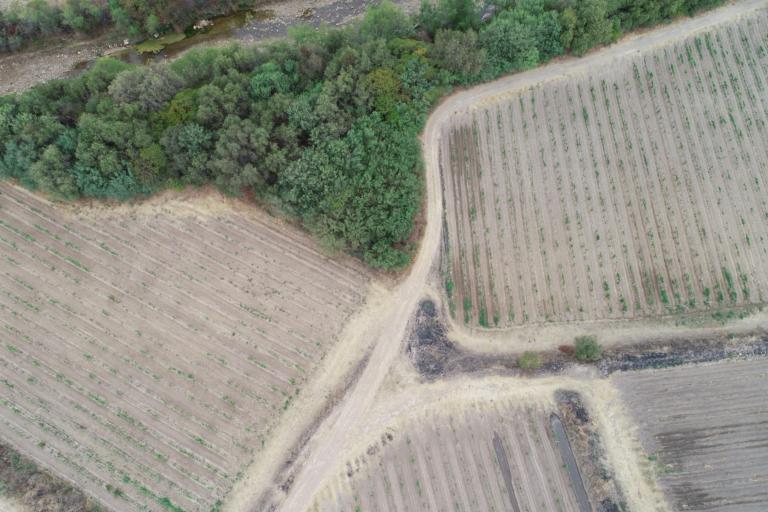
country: BO
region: Tarija
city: Tarija
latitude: -21.6005
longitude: -64.6219
